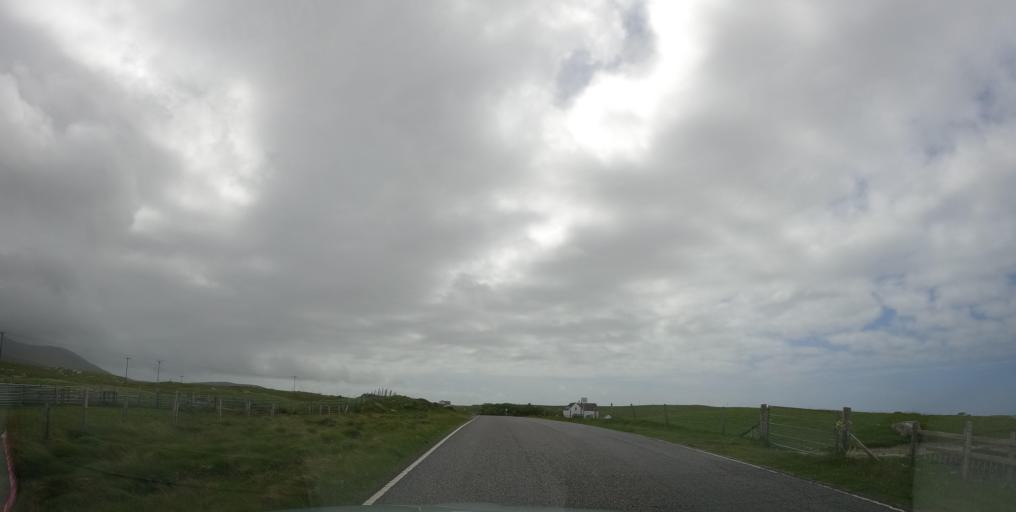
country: GB
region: Scotland
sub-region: Eilean Siar
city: Isle of South Uist
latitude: 57.2913
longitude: -7.3666
